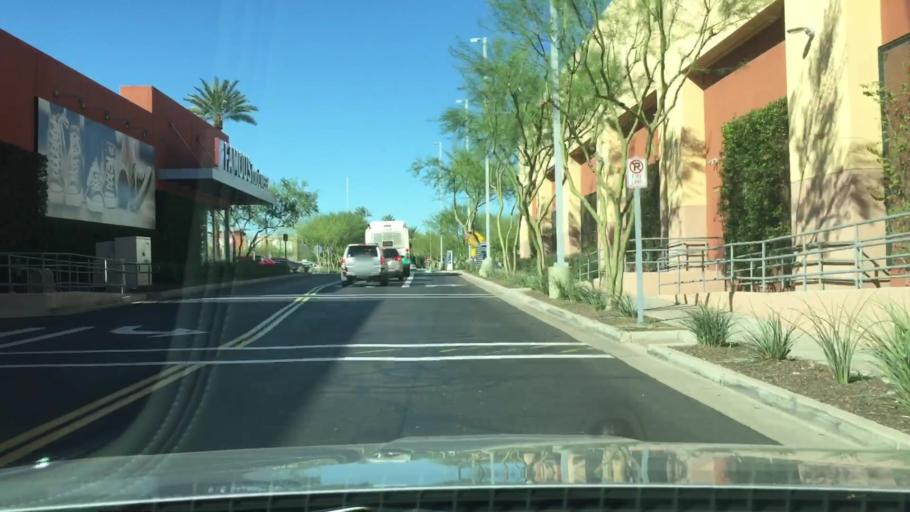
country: US
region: Arizona
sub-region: Maricopa County
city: Tempe
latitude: 33.4298
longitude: -111.9048
